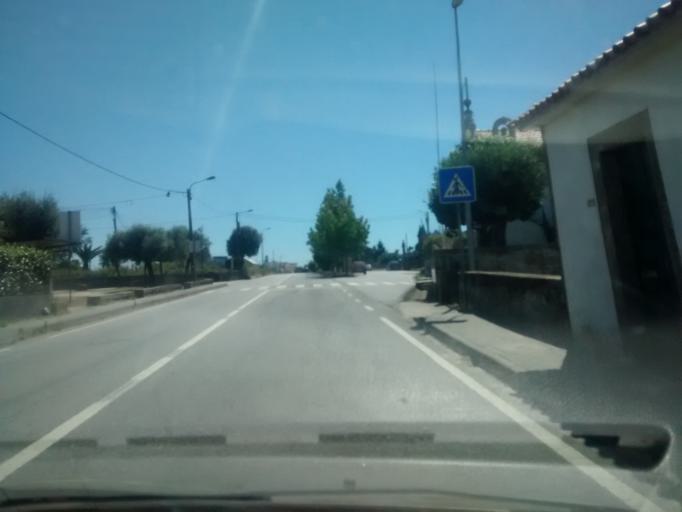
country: PT
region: Braga
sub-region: Barcelos
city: Vila Frescainha
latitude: 41.5077
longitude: -8.6636
